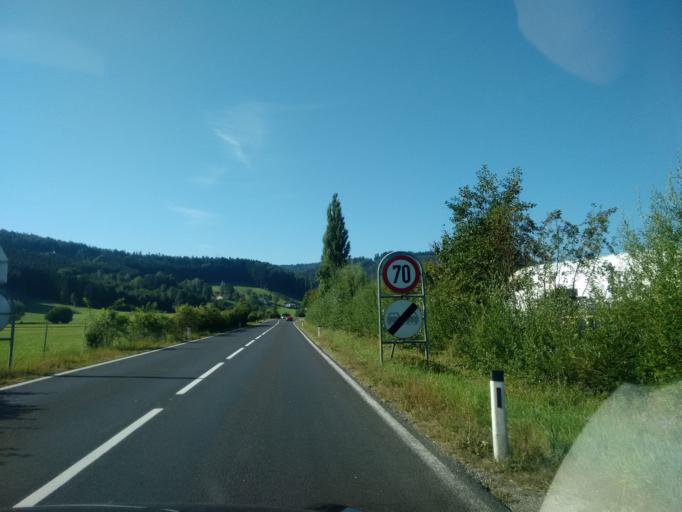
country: AT
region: Upper Austria
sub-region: Politischer Bezirk Vocklabruck
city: Seewalchen
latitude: 47.9426
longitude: 13.6105
